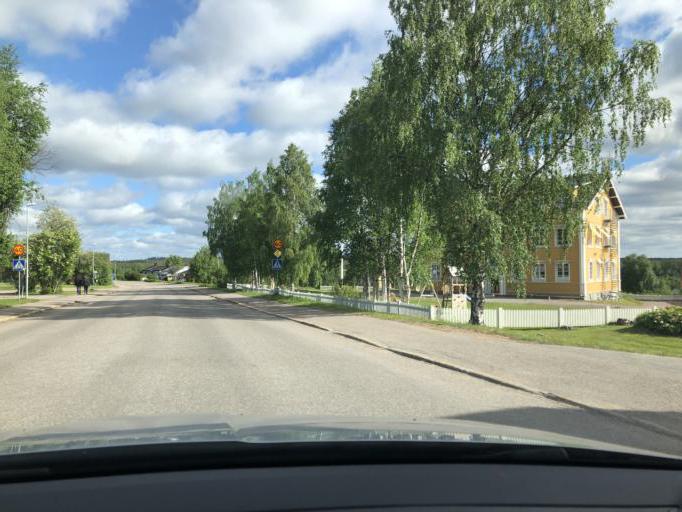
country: SE
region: Norrbotten
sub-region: Pajala Kommun
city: Pajala
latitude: 67.2136
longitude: 23.3669
